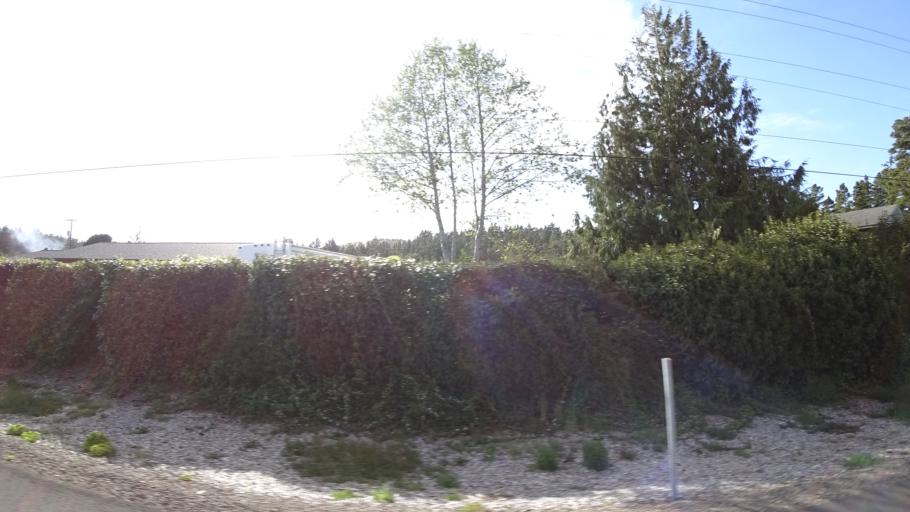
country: US
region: Oregon
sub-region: Lane County
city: Dunes City
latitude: 43.9039
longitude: -124.1151
